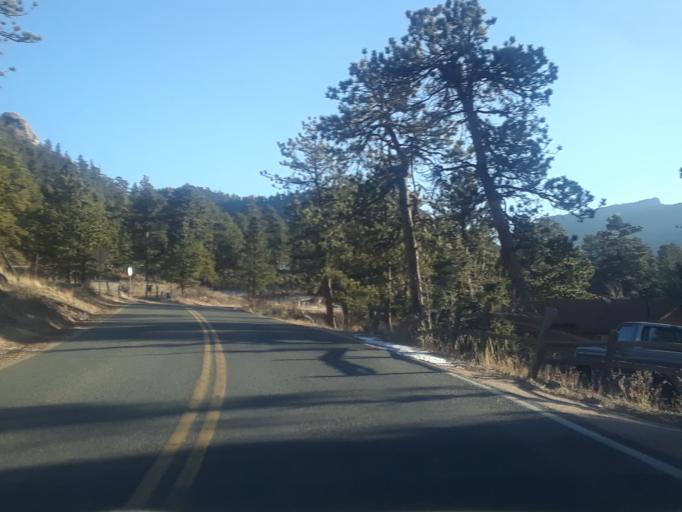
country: US
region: Colorado
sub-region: Larimer County
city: Estes Park
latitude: 40.3642
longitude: -105.5369
